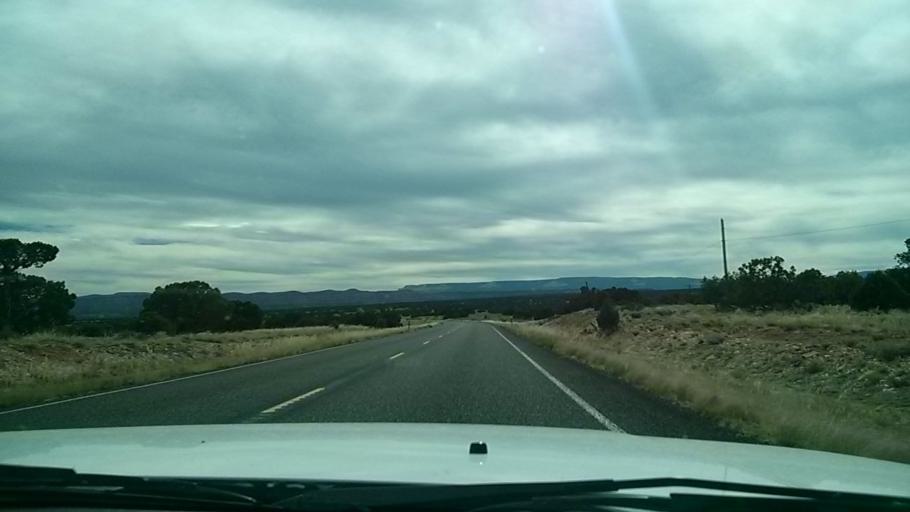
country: US
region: Utah
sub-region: Wayne County
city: Loa
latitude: 37.7494
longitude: -111.4838
